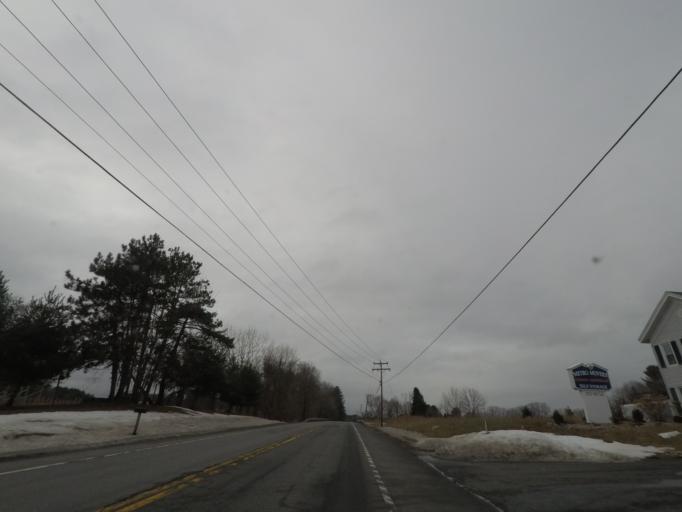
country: US
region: New York
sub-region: Schenectady County
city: Rotterdam
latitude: 42.7265
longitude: -73.9626
